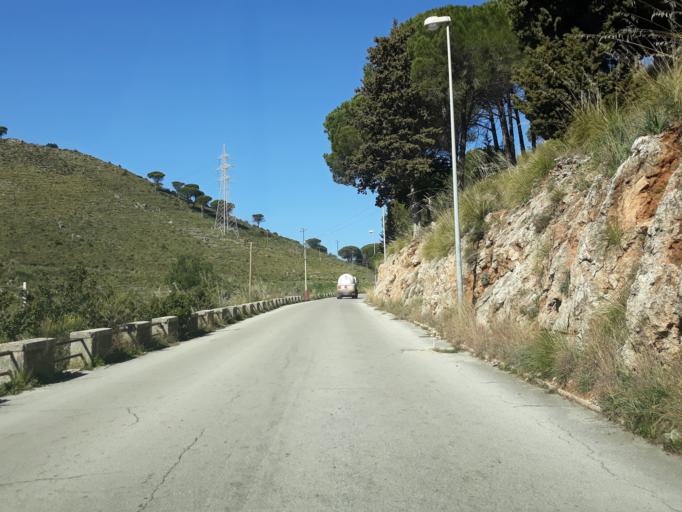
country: IT
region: Sicily
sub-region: Palermo
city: Cannizzaro-Favara
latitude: 38.0803
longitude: 13.2740
